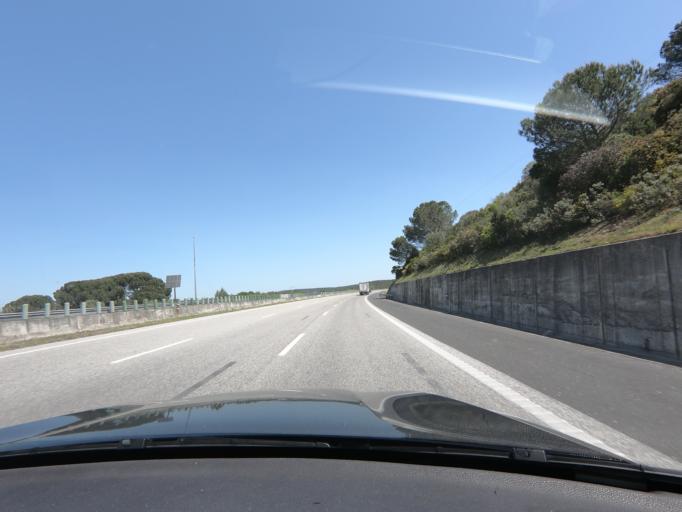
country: PT
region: Lisbon
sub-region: Alenquer
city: Carregado
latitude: 39.0663
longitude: -8.9387
